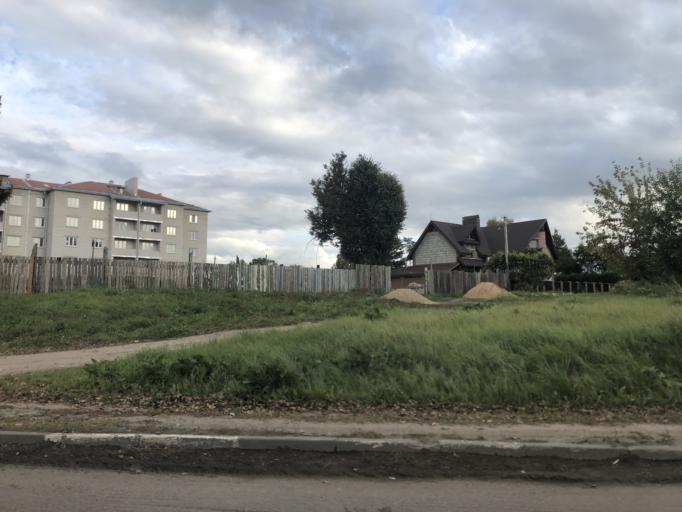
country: RU
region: Tverskaya
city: Rzhev
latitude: 56.2528
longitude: 34.3134
